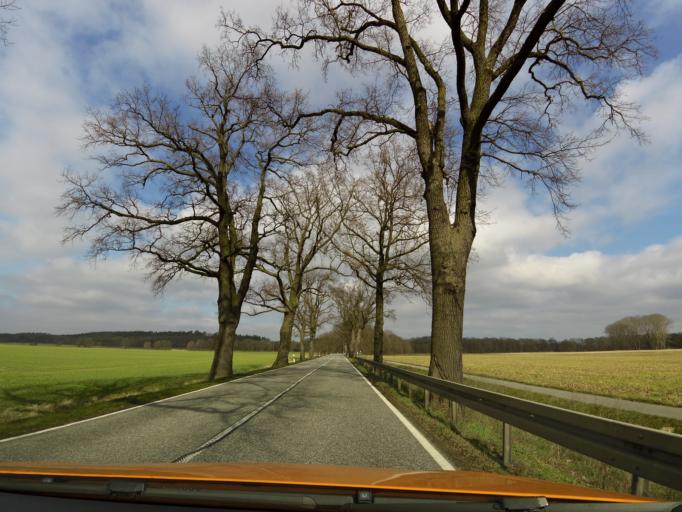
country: DE
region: Brandenburg
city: Rhinow
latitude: 52.6822
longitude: 12.3582
